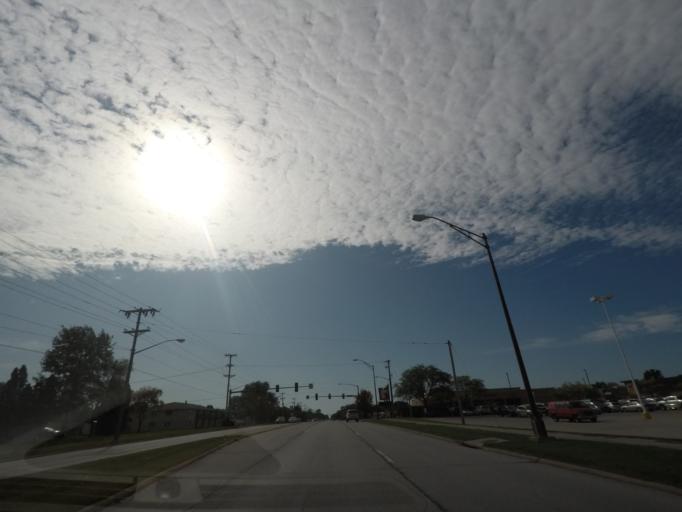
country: US
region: Iowa
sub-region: Story County
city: Ames
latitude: 42.0498
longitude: -93.6206
